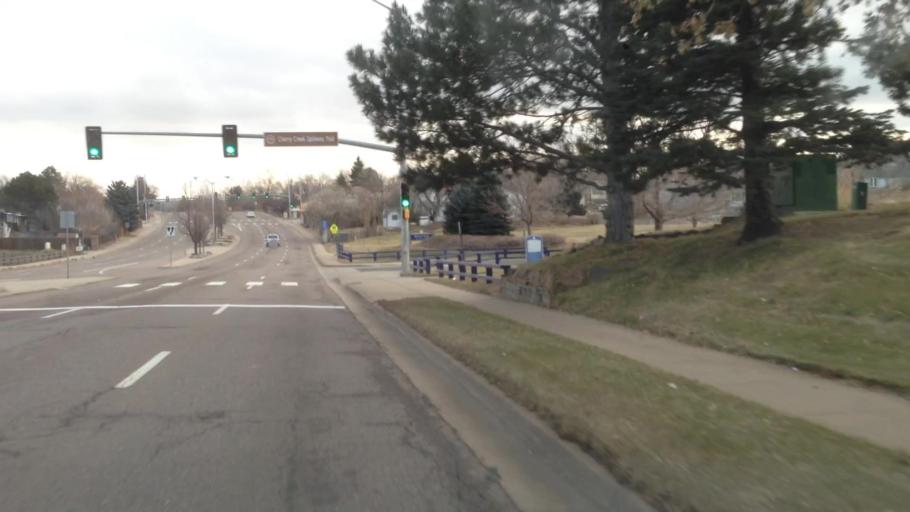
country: US
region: Colorado
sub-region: Adams County
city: Aurora
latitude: 39.6740
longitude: -104.8041
